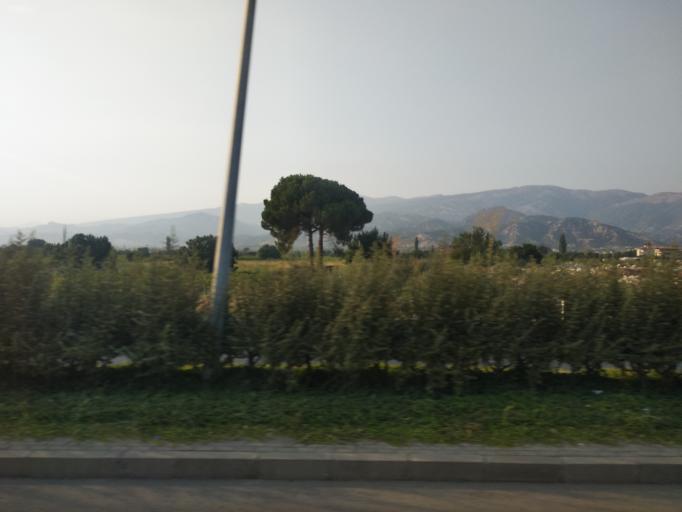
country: TR
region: Manisa
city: Salihli
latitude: 38.4933
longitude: 28.1734
